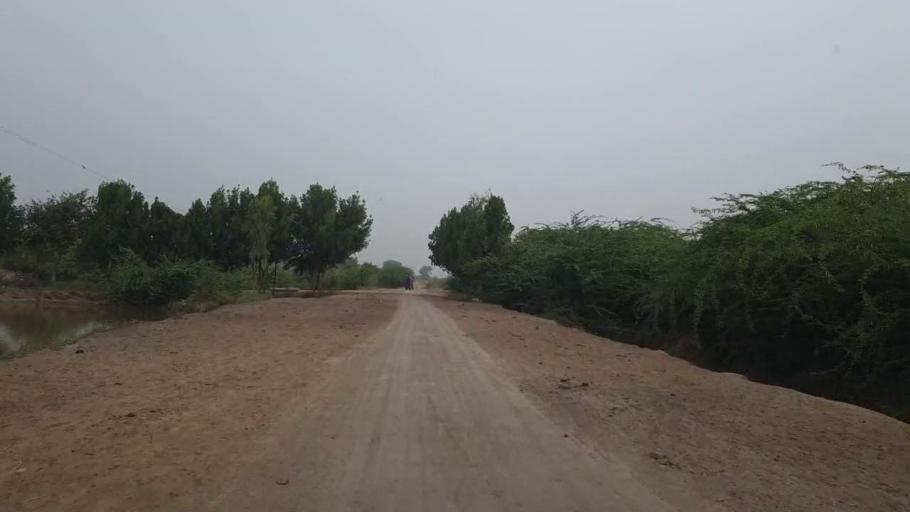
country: PK
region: Sindh
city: Badin
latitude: 24.5870
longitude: 68.6668
